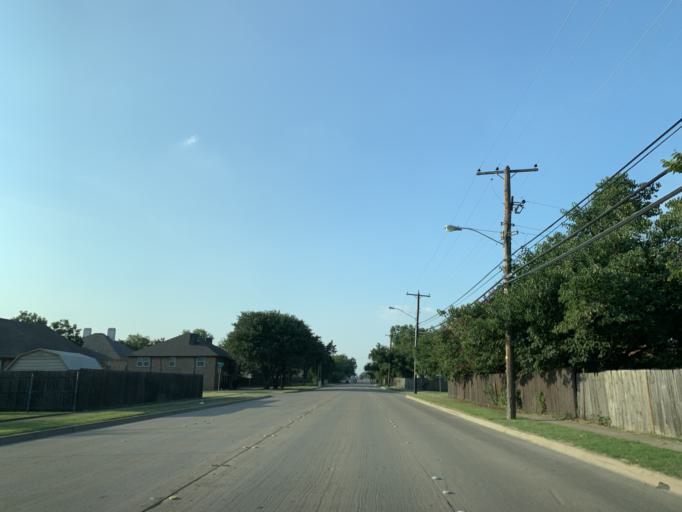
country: US
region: Texas
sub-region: Tarrant County
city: Hurst
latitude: 32.8122
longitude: -97.1866
